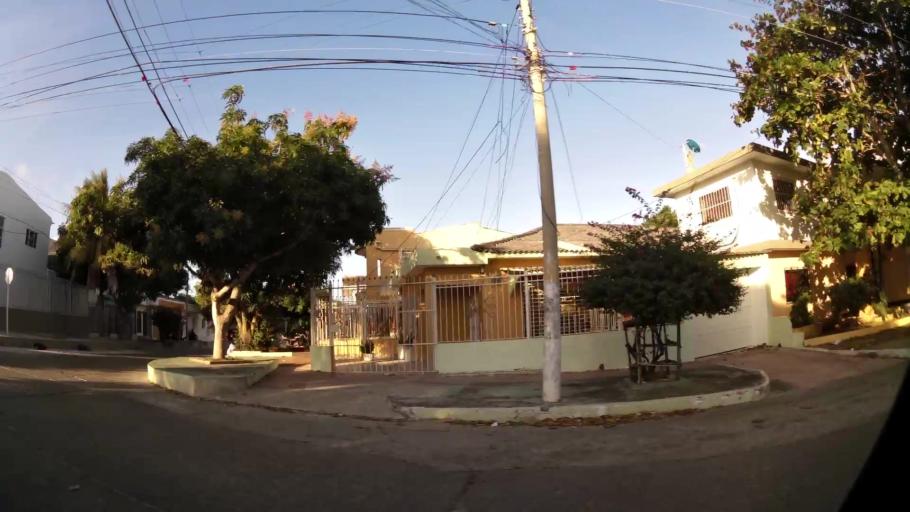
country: CO
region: Atlantico
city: Barranquilla
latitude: 10.9854
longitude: -74.8012
